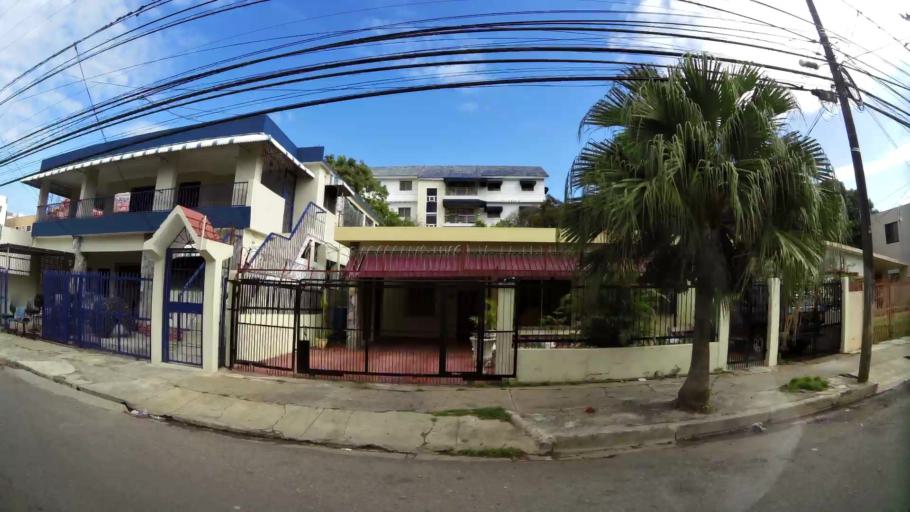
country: DO
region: Santo Domingo
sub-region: Santo Domingo
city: Santo Domingo Este
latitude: 18.4862
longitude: -69.8675
